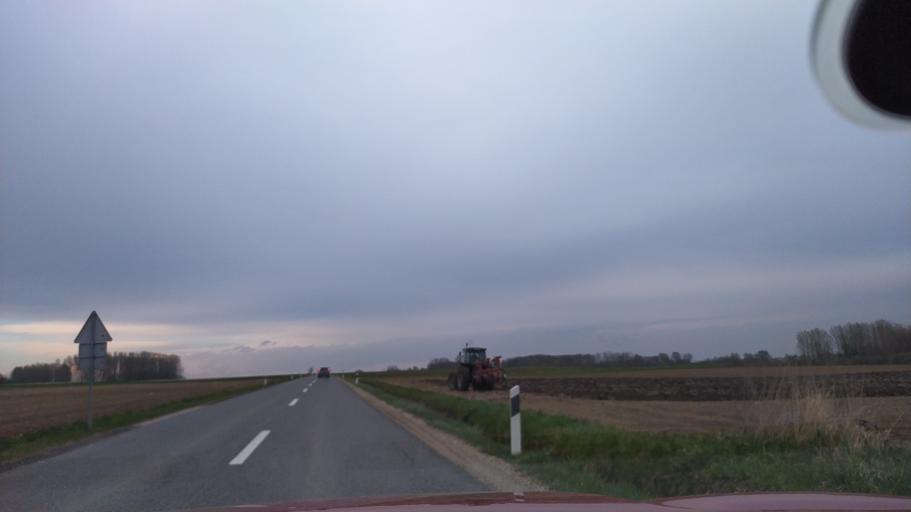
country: HR
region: Varazdinska
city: Ludbreg
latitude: 46.2426
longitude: 16.5532
